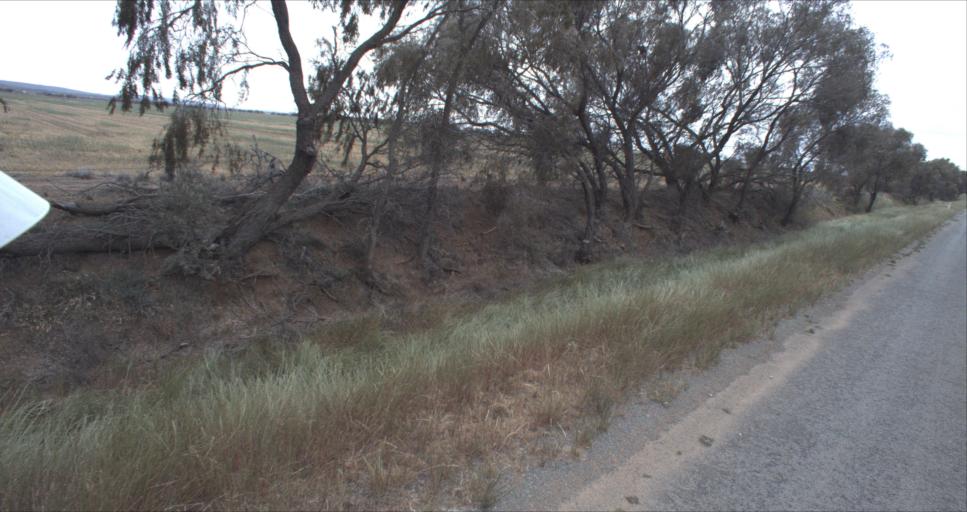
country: AU
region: New South Wales
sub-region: Leeton
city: Leeton
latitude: -34.4303
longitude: 146.3368
